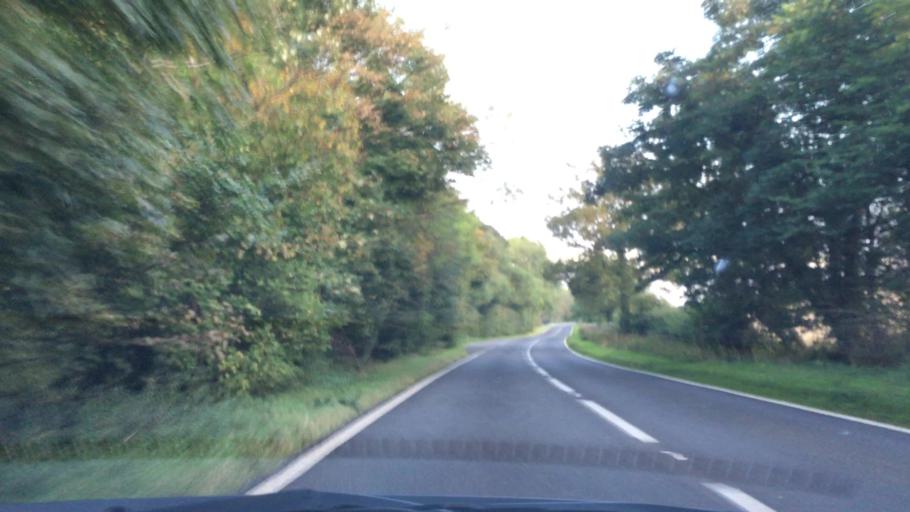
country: GB
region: England
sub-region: North East Lincolnshire
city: Wold Newton
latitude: 53.4736
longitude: -0.1126
